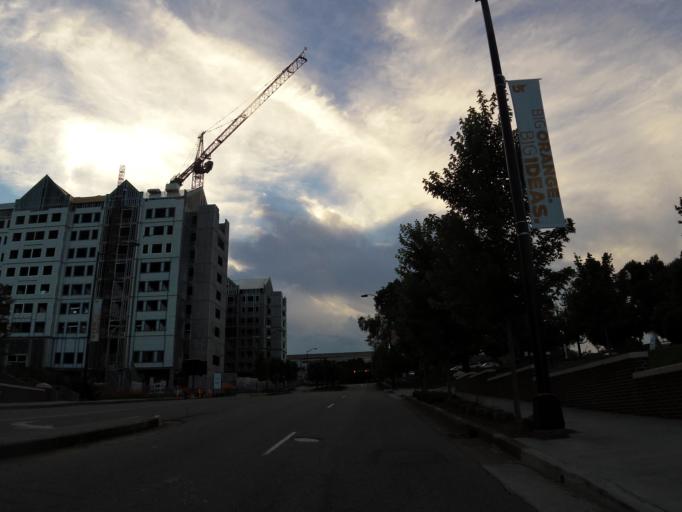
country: US
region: Tennessee
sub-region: Knox County
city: Knoxville
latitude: 35.9513
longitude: -83.9274
